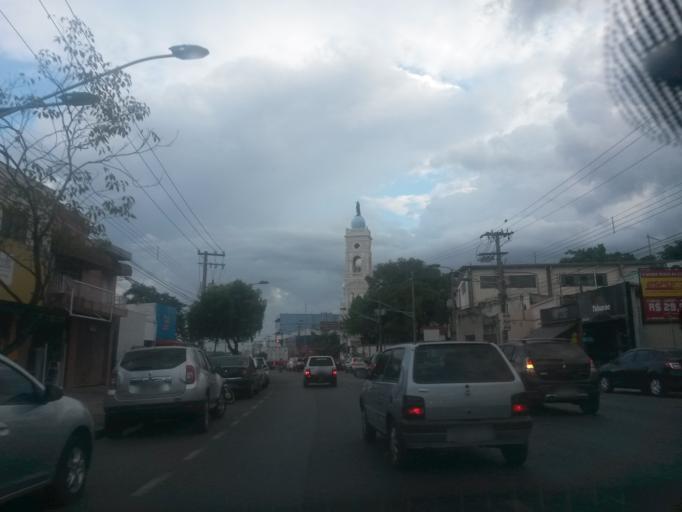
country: BR
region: Mato Grosso
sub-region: Cuiaba
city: Cuiaba
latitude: -15.6102
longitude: -56.1027
